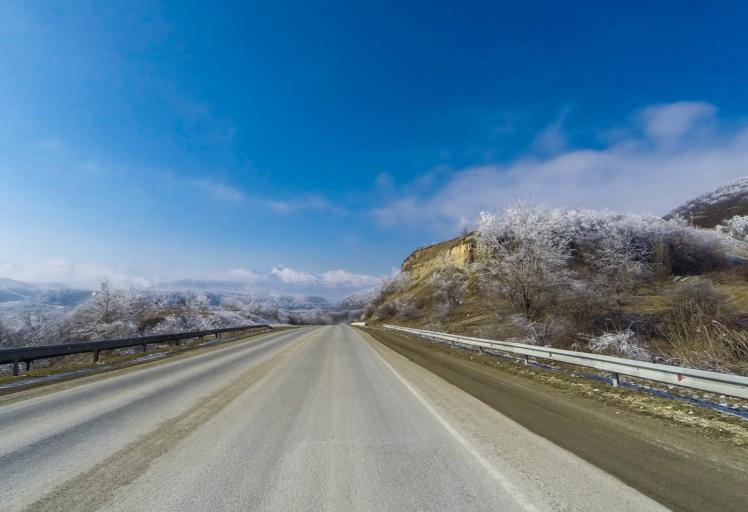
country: RU
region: Kabardino-Balkariya
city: Zhemtala
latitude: 43.3381
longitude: 43.6609
